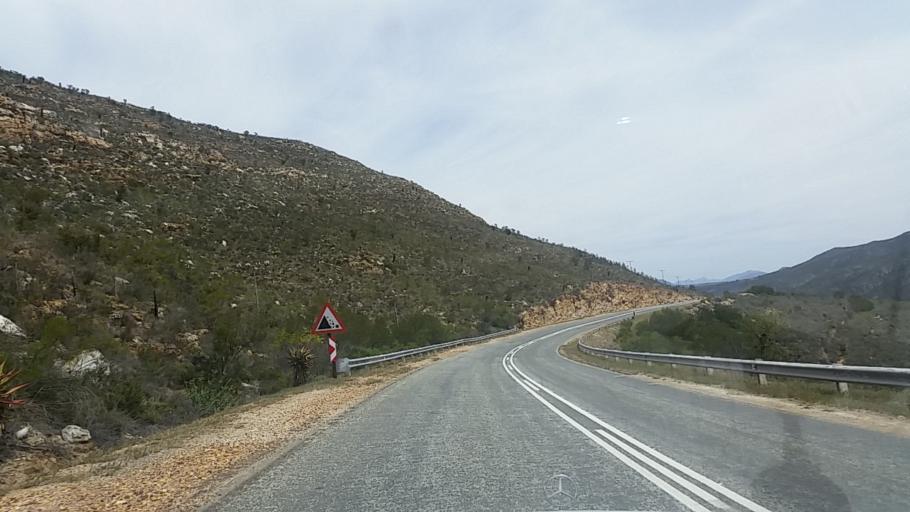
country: ZA
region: Western Cape
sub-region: Eden District Municipality
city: Knysna
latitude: -33.7478
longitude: 22.9798
